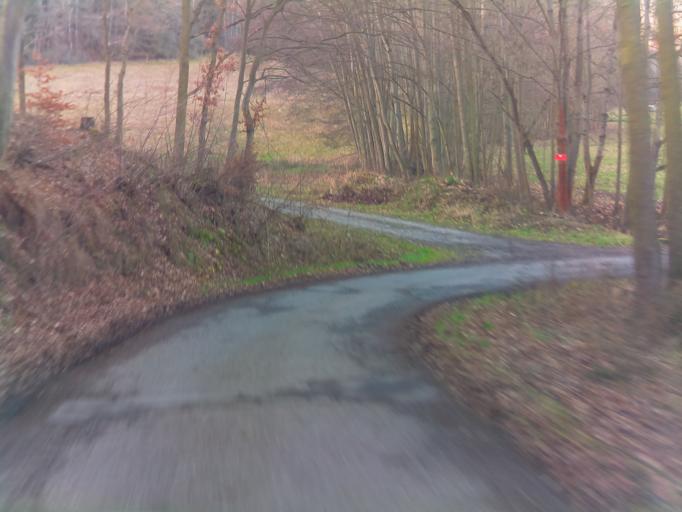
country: DE
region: Thuringia
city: Rudolstadt
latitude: 50.7650
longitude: 11.3535
